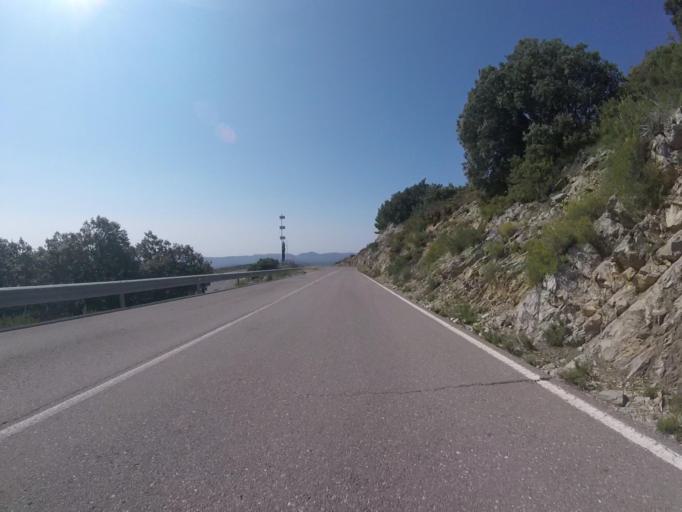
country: ES
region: Valencia
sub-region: Provincia de Castello
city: Benafigos
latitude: 40.2645
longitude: -0.2328
